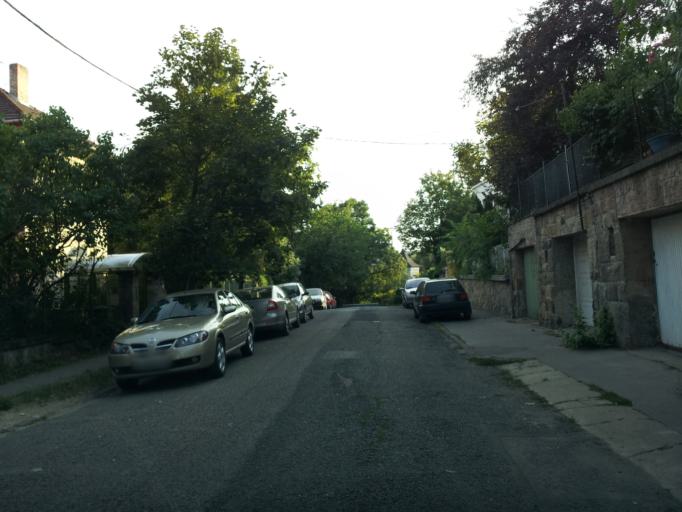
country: HU
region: Budapest
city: Budapest XII. keruelet
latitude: 47.4991
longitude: 19.0157
